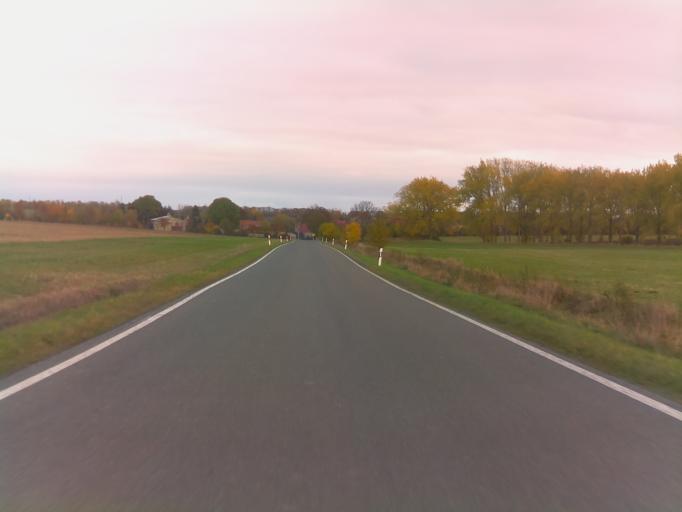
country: DE
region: Thuringia
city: Milda
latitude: 50.8398
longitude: 11.4079
